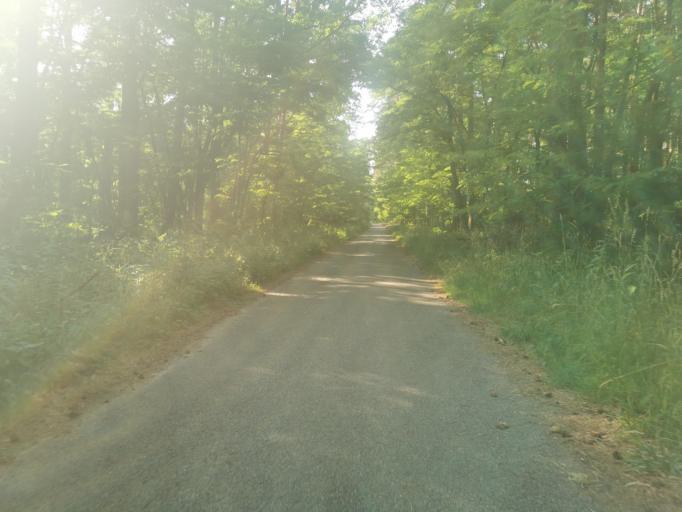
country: CZ
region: South Moravian
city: Vacenovice
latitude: 48.9316
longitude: 17.1903
